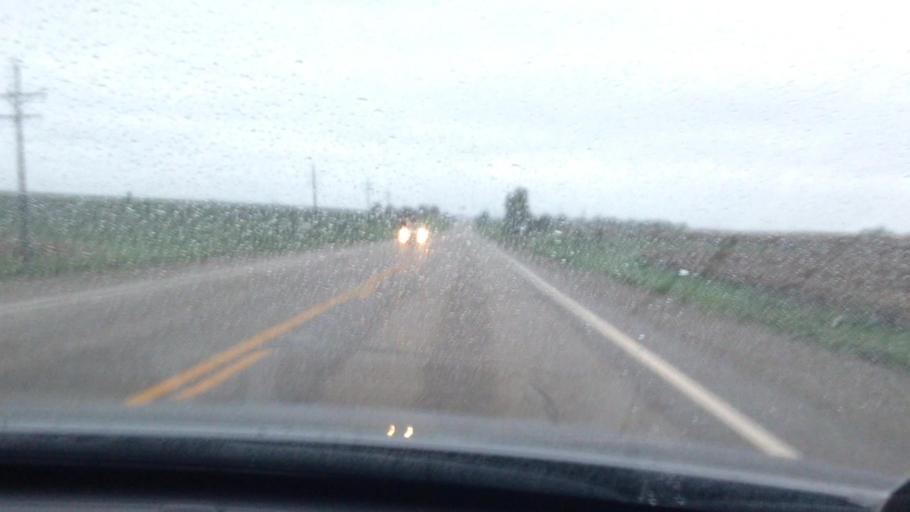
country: US
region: Kansas
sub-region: Brown County
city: Hiawatha
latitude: 39.8141
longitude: -95.5273
